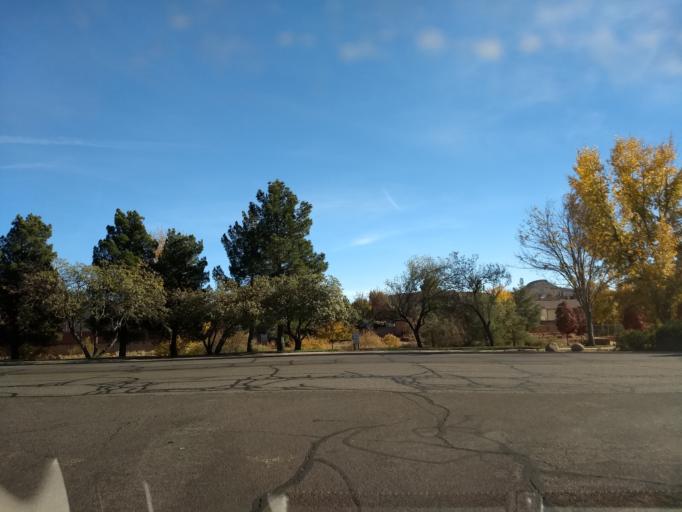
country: US
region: Utah
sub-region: Washington County
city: Santa Clara
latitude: 37.1308
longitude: -113.6147
